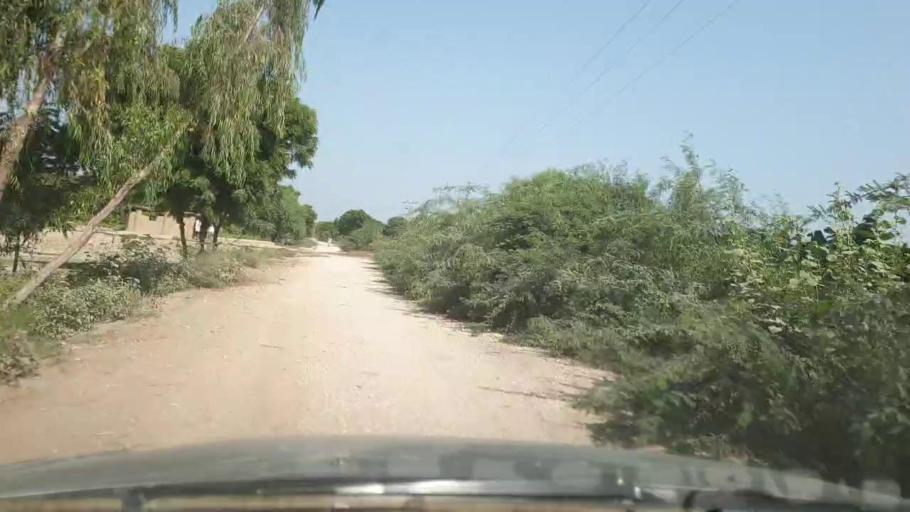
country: PK
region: Sindh
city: Tando Ghulam Ali
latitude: 25.1938
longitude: 68.8854
